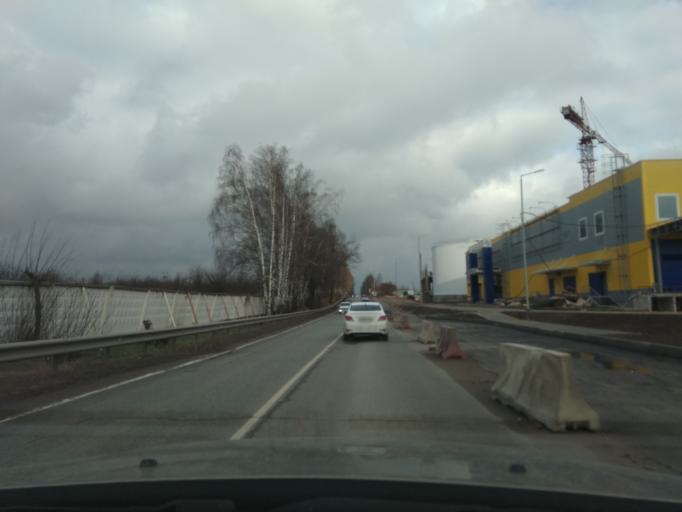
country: RU
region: Moscow
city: Biryulevo
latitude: 55.5666
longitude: 37.6883
